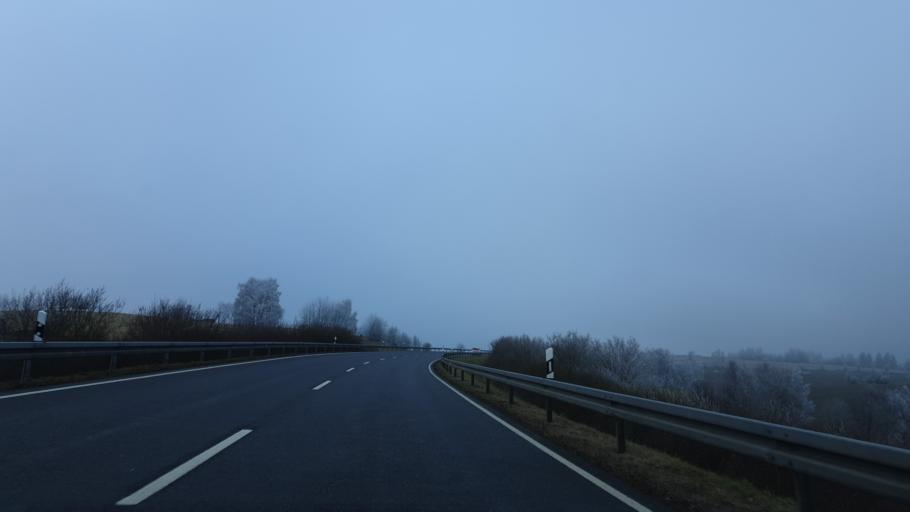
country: DE
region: Saxony
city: Bad Brambach
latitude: 50.2252
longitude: 12.3210
